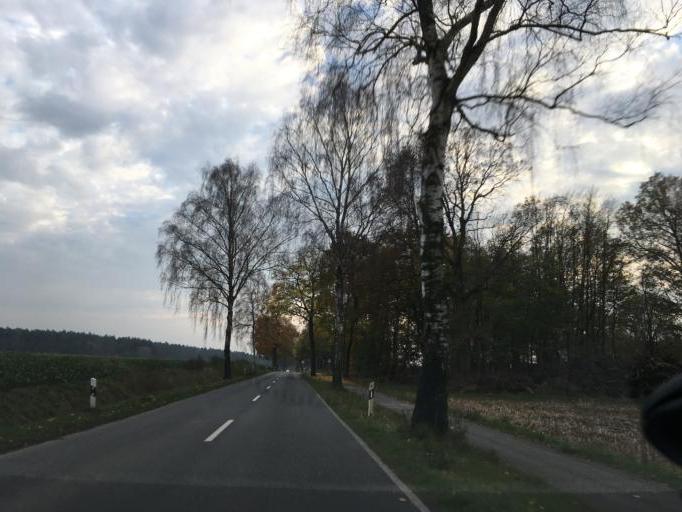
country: DE
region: Lower Saxony
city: Wietzendorf
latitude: 52.8931
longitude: 9.9840
